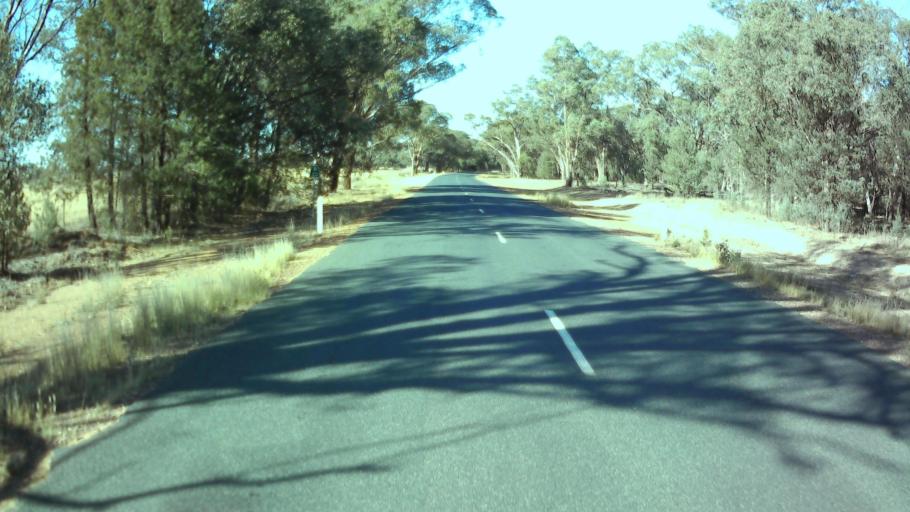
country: AU
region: New South Wales
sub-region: Weddin
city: Grenfell
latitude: -34.0161
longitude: 148.1094
